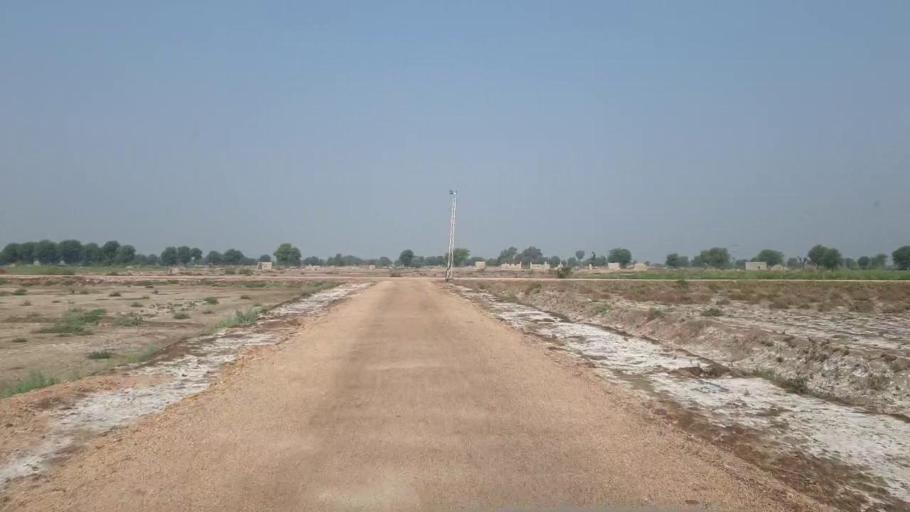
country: PK
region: Sindh
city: Umarkot
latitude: 25.4169
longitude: 69.6773
